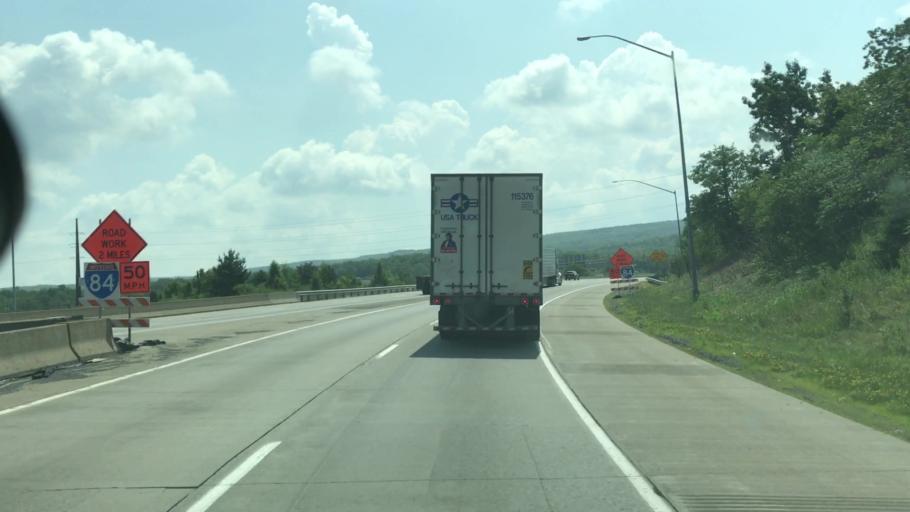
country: US
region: Pennsylvania
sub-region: Lackawanna County
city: Dunmore
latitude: 41.4198
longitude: -75.6061
